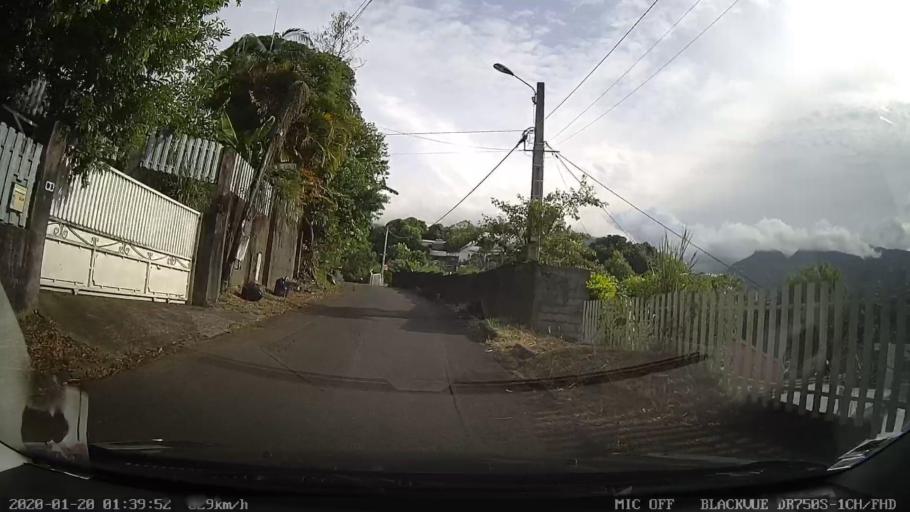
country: RE
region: Reunion
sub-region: Reunion
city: Sainte-Marie
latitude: -20.9203
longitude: 55.5153
